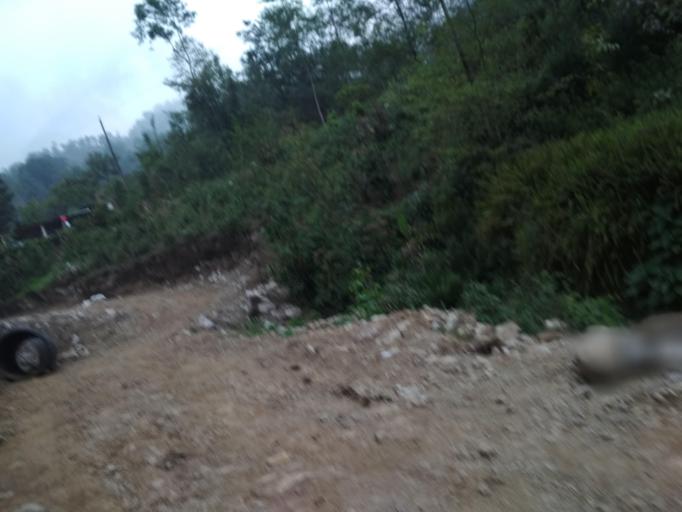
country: MX
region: Veracruz
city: La Perla
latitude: 18.9295
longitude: -97.1501
